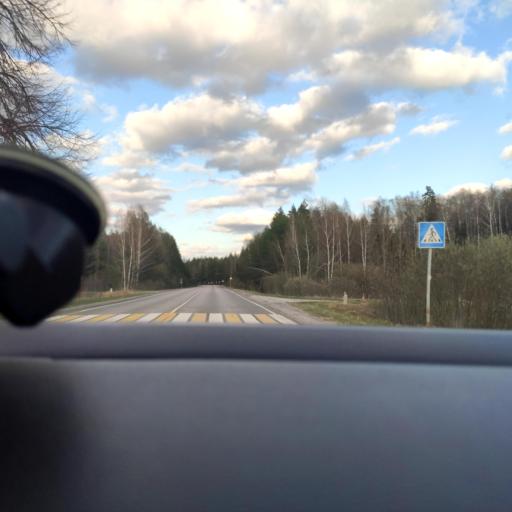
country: RU
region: Moskovskaya
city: Shaturtorf
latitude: 55.4286
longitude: 39.3459
